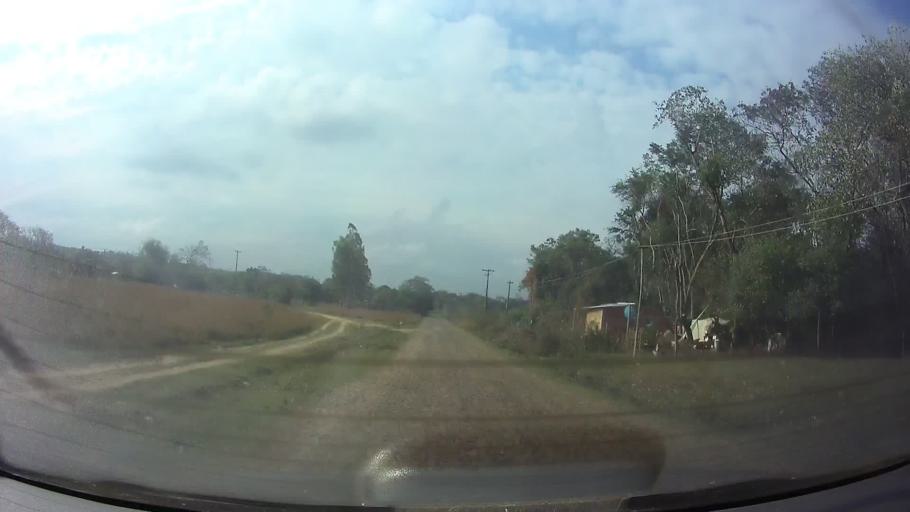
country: PY
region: Cordillera
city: Arroyos y Esteros
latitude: -25.0004
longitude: -57.1954
